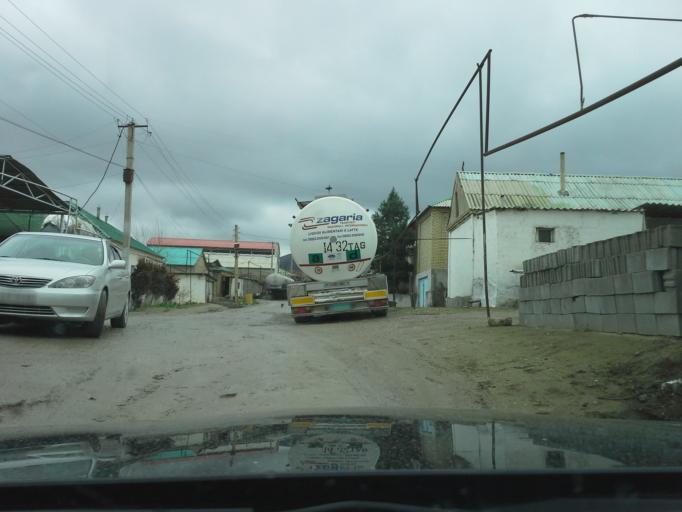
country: TM
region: Ahal
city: Abadan
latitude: 37.9586
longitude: 58.2118
